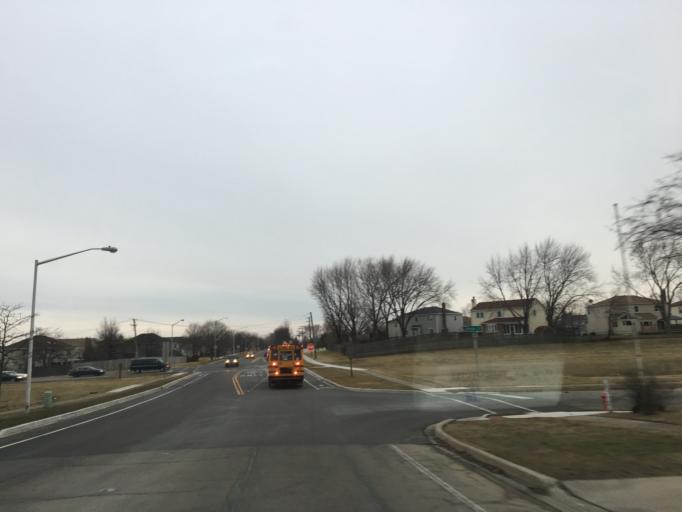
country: US
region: Illinois
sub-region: Cook County
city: Schaumburg
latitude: 42.0364
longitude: -88.1094
